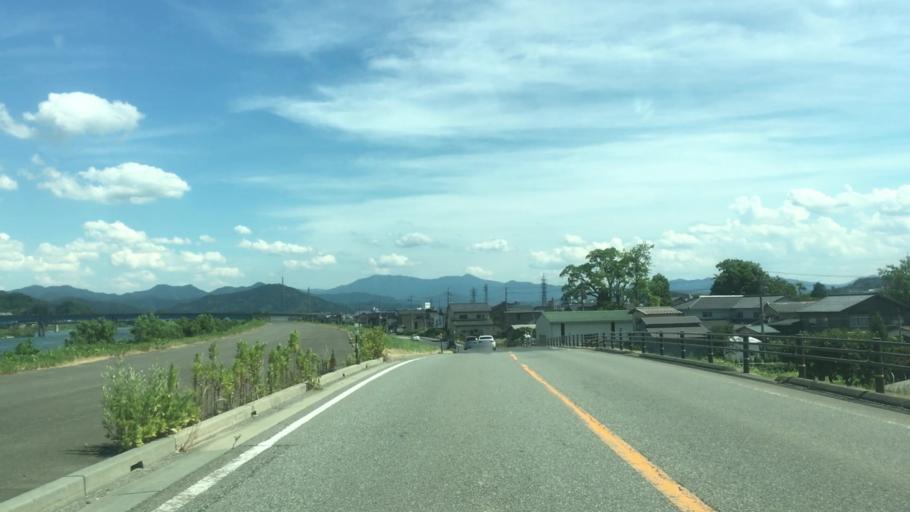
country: JP
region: Hyogo
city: Toyooka
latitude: 35.5609
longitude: 134.8143
